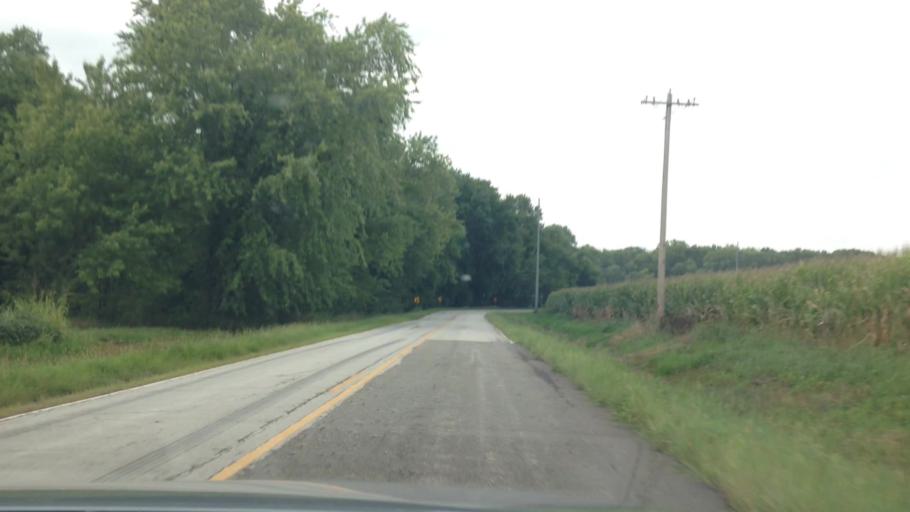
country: US
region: Missouri
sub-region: Clay County
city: Smithville
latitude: 39.4023
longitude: -94.6619
